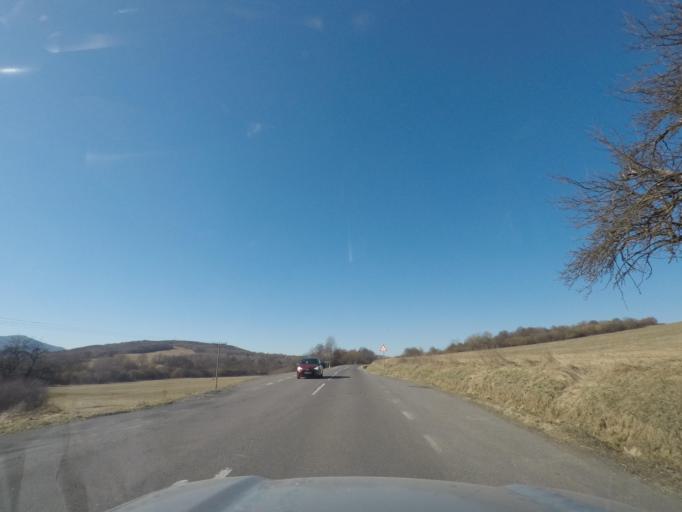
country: UA
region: Zakarpattia
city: Velykyi Bereznyi
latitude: 48.9065
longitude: 22.3756
